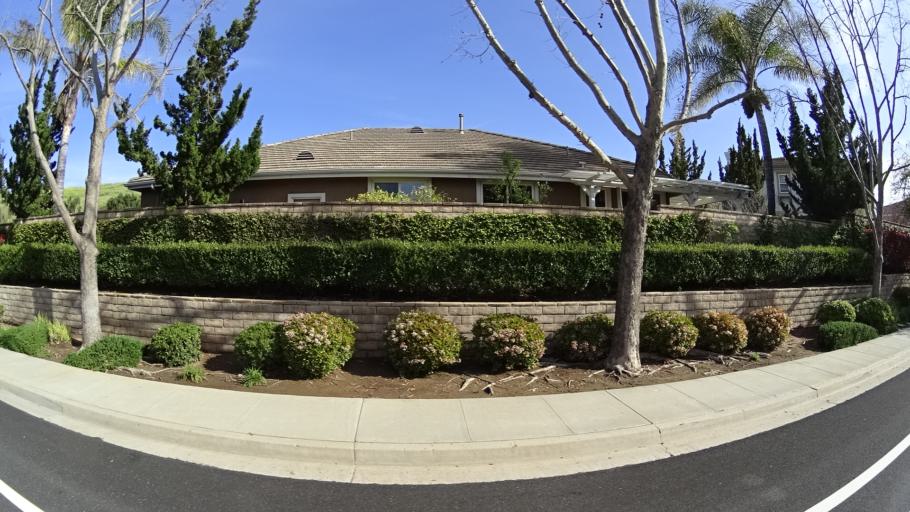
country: US
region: California
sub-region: Ventura County
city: Thousand Oaks
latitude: 34.2144
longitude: -118.8248
